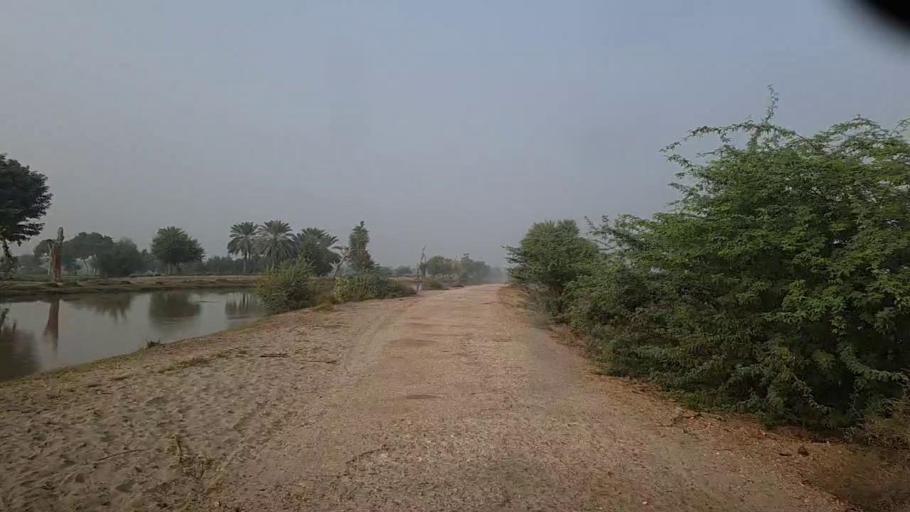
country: PK
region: Sindh
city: Bozdar
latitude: 27.1517
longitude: 68.6604
